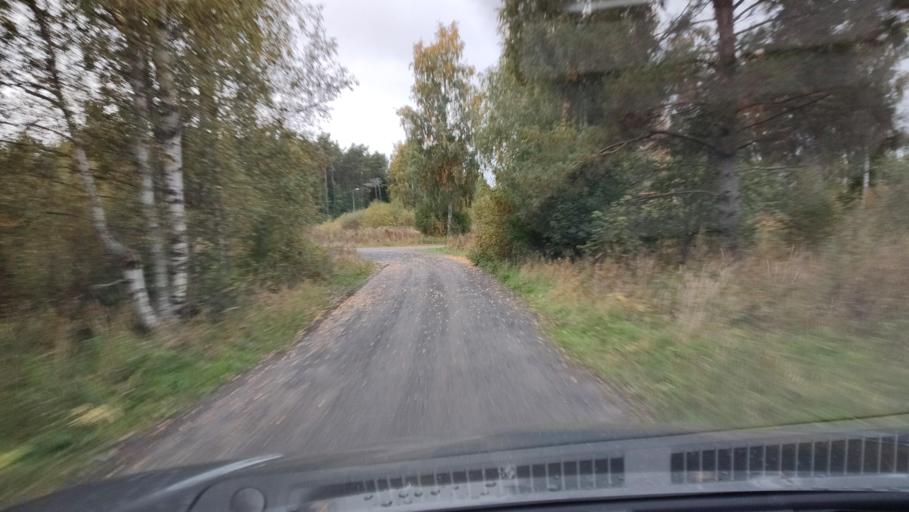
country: FI
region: Ostrobothnia
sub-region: Sydosterbotten
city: Kristinestad
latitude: 62.2764
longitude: 21.4021
